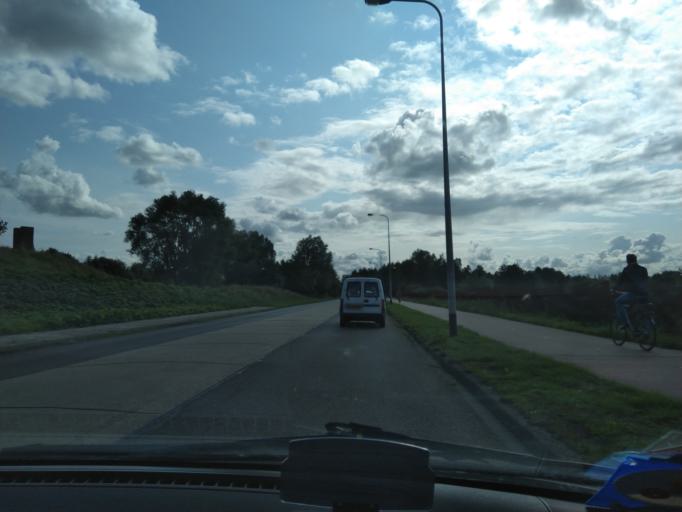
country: NL
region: Groningen
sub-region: Gemeente Groningen
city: Groningen
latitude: 53.1875
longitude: 6.5446
